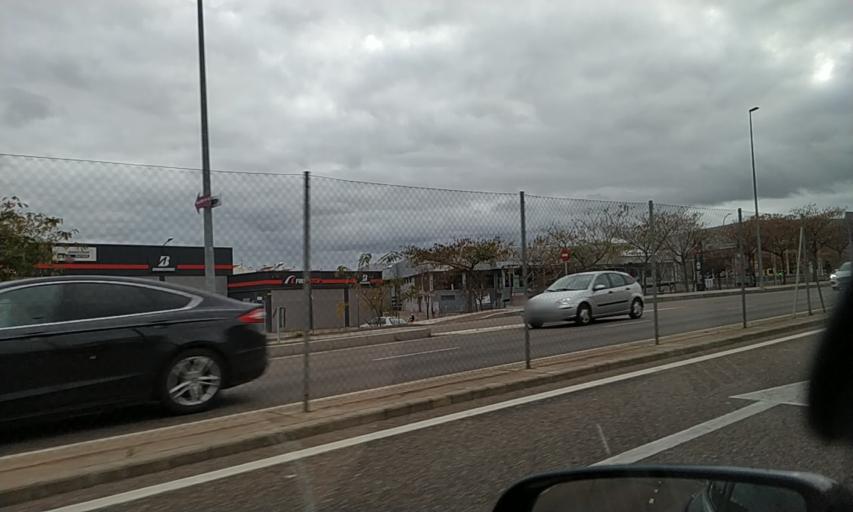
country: ES
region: Extremadura
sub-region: Provincia de Badajoz
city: Badajoz
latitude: 38.8757
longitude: -6.9528
